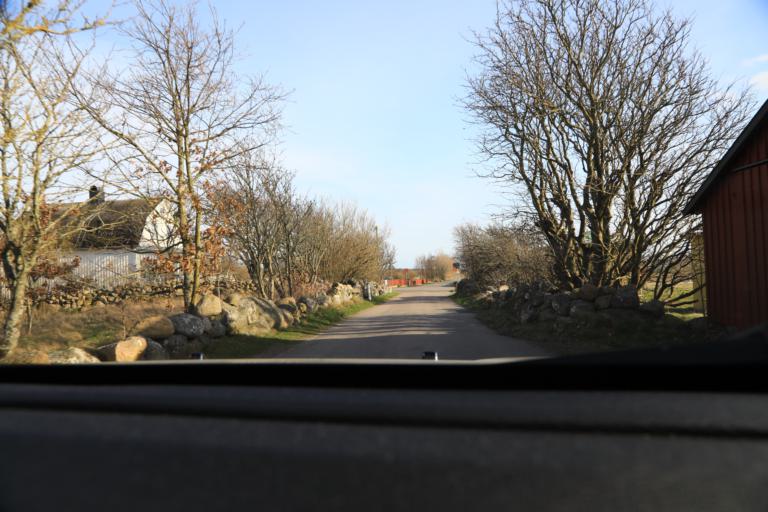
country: SE
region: Halland
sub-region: Varbergs Kommun
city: Varberg
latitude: 57.1199
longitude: 12.2152
